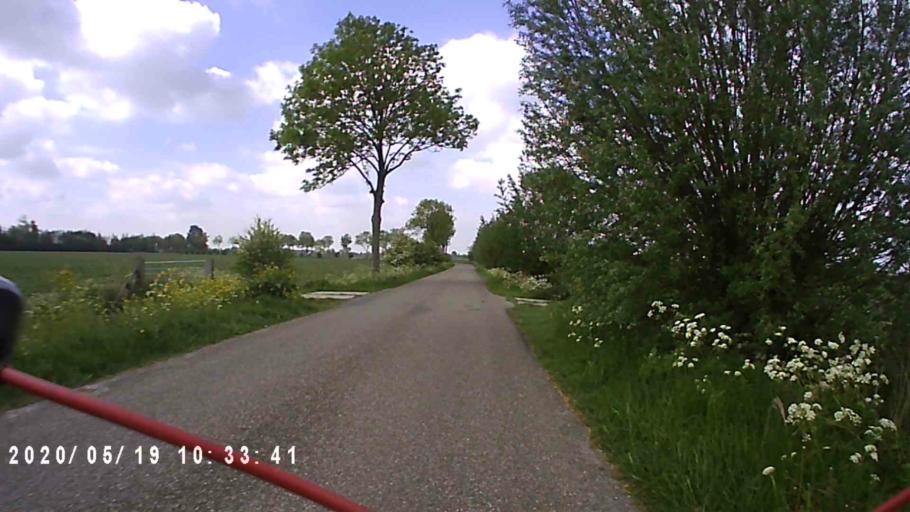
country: NL
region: Friesland
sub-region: Gemeente Kollumerland en Nieuwkruisland
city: Kollum
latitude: 53.2867
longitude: 6.1872
